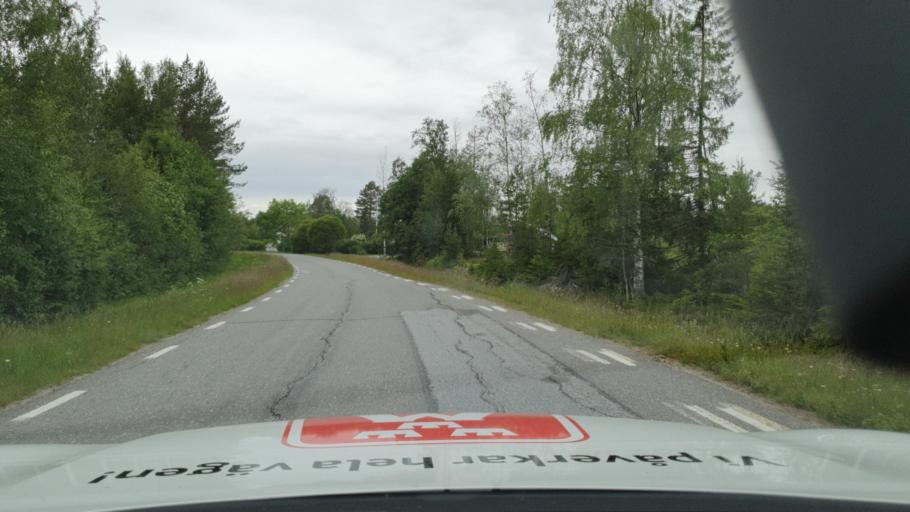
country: SE
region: Vaesterbotten
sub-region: Nordmalings Kommun
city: Nordmaling
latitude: 63.4958
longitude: 19.4338
